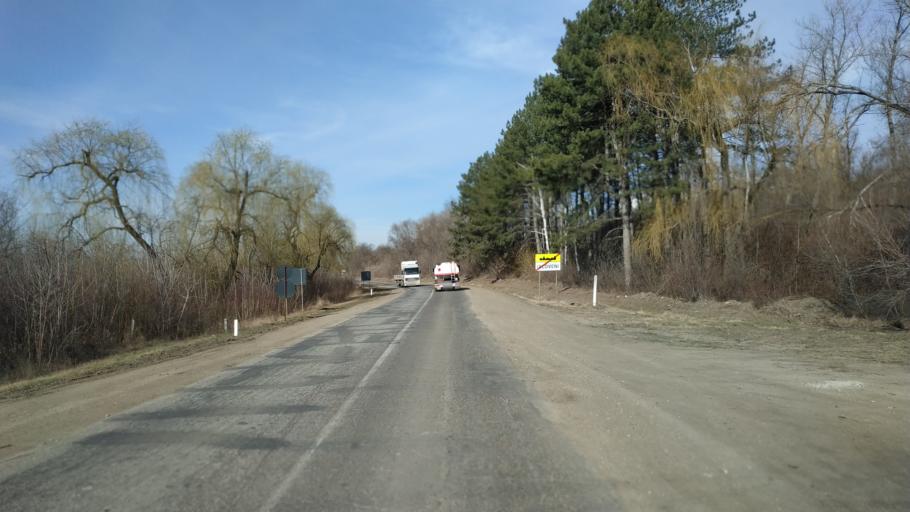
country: MD
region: Laloveni
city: Ialoveni
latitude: 46.9522
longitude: 28.7632
